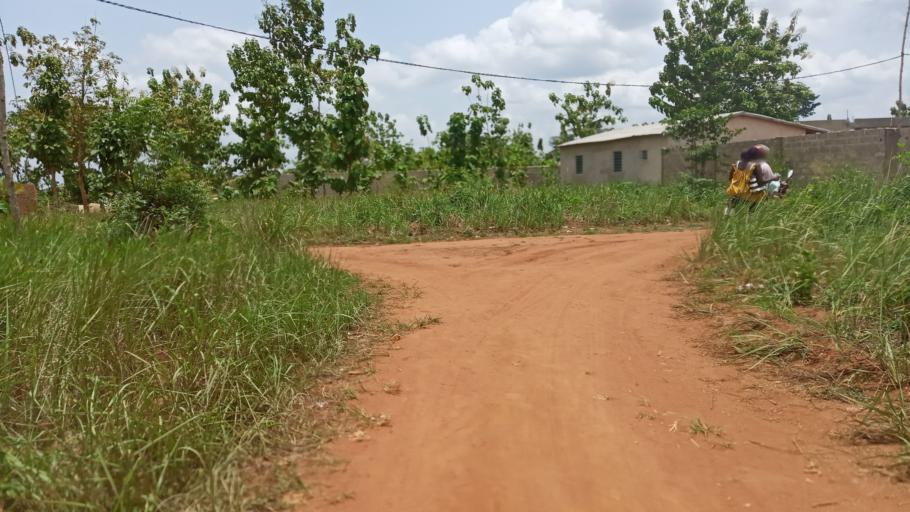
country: TG
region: Maritime
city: Tsevie
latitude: 6.2942
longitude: 1.1330
